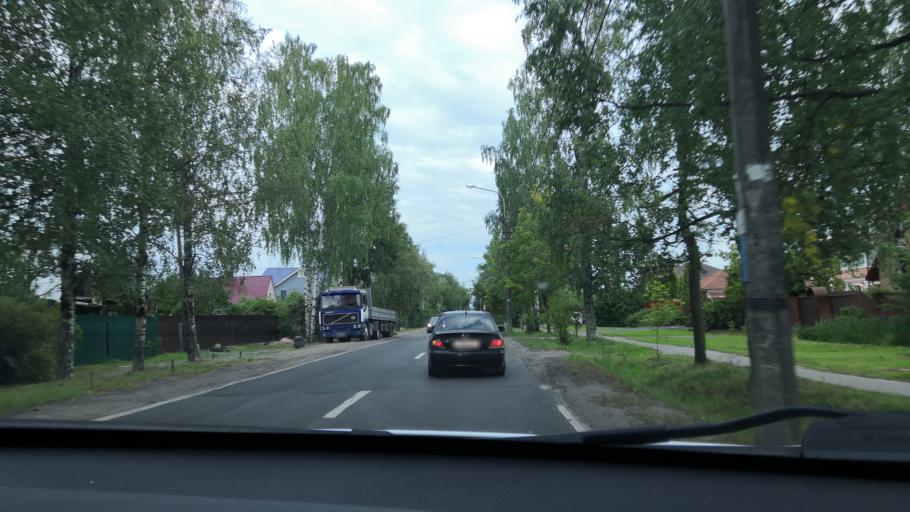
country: RU
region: St.-Petersburg
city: Pushkin
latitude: 59.7020
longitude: 30.4078
